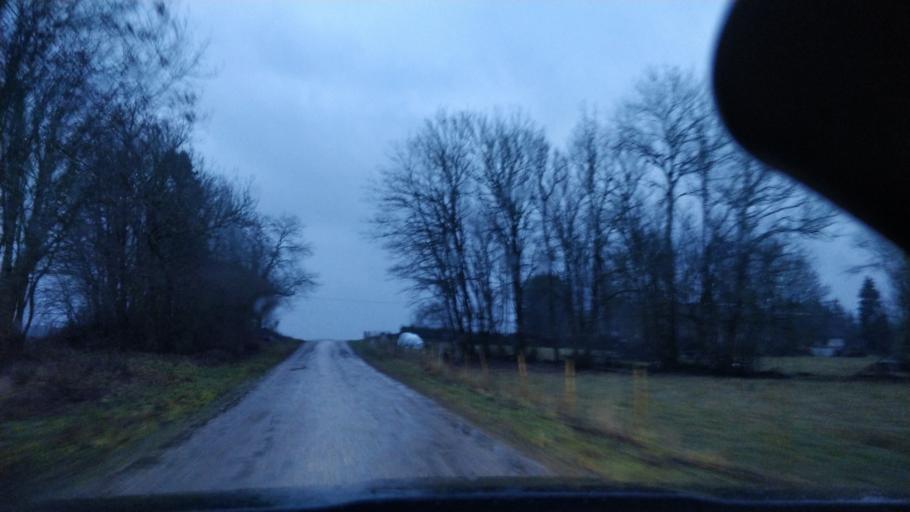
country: EE
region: Laeaene
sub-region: Lihula vald
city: Lihula
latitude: 58.8491
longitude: 23.9840
